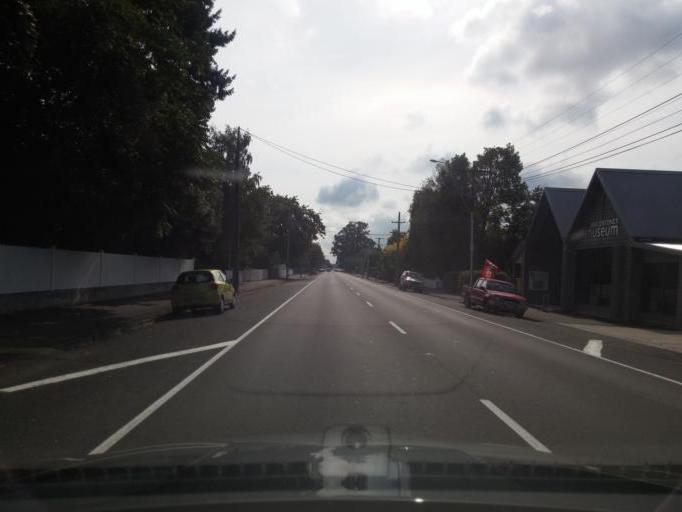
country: NZ
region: Wellington
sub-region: Masterton District
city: Masterton
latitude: -41.0852
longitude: 175.4549
